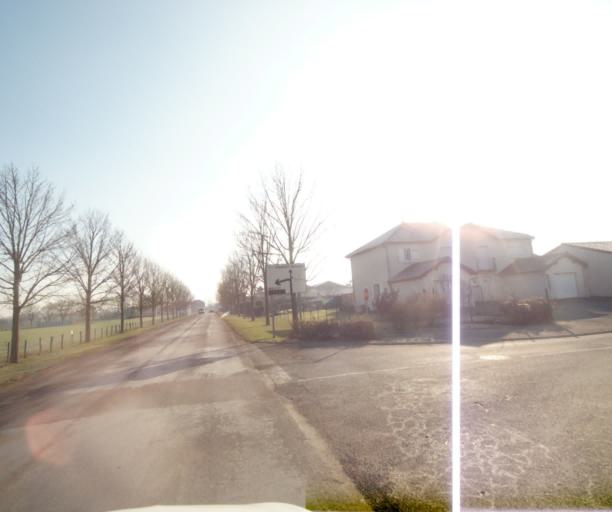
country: FR
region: Champagne-Ardenne
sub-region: Departement de la Haute-Marne
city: Montier-en-Der
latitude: 48.4749
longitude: 4.7825
